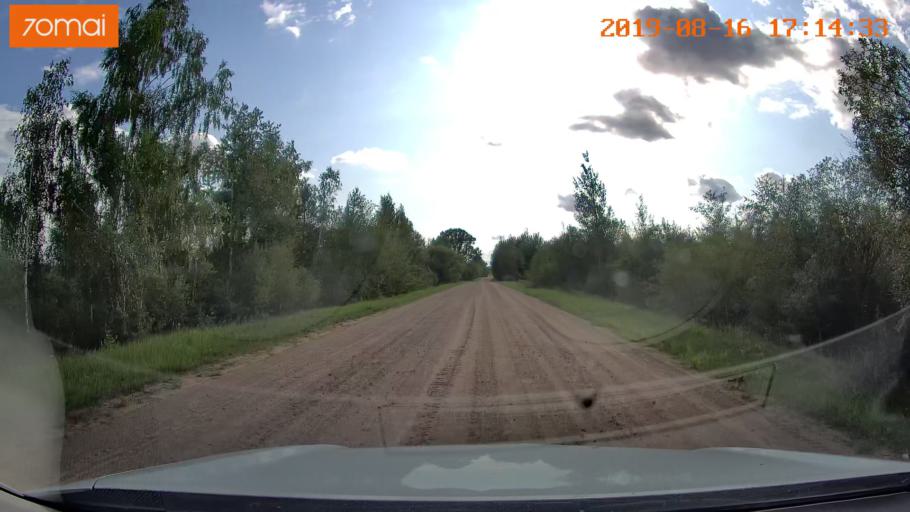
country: BY
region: Mogilev
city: Hlusha
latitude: 53.1835
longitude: 28.8567
